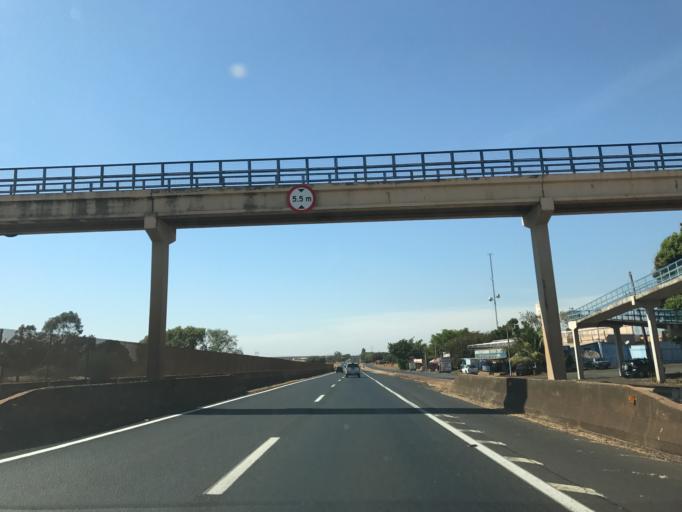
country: BR
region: Minas Gerais
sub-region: Centralina
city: Centralina
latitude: -18.7127
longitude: -49.1346
